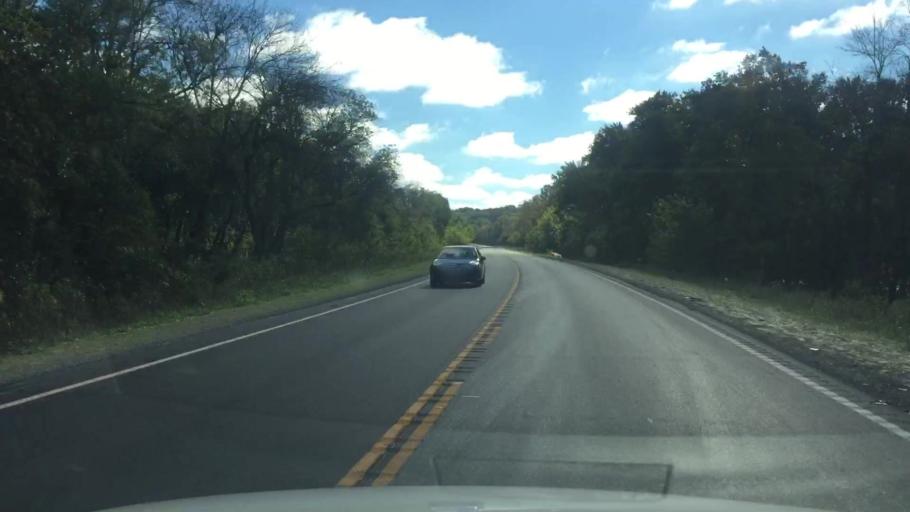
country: US
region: Missouri
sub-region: Howard County
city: New Franklin
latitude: 38.9873
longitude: -92.5549
